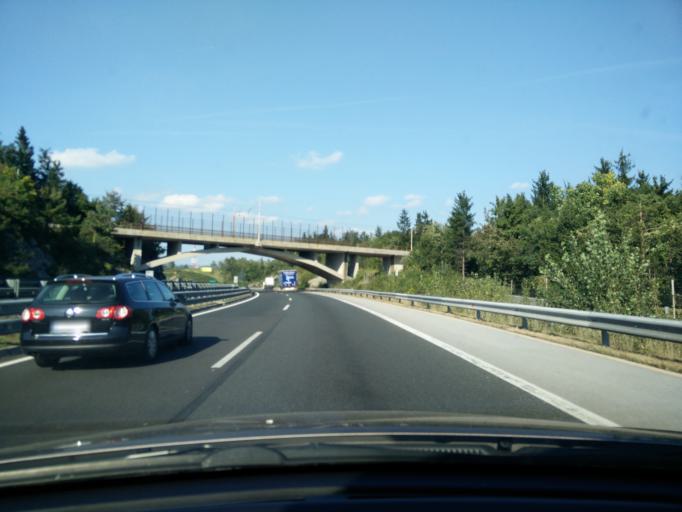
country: SI
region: Cerknica
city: Rakek
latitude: 45.8101
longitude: 14.2846
